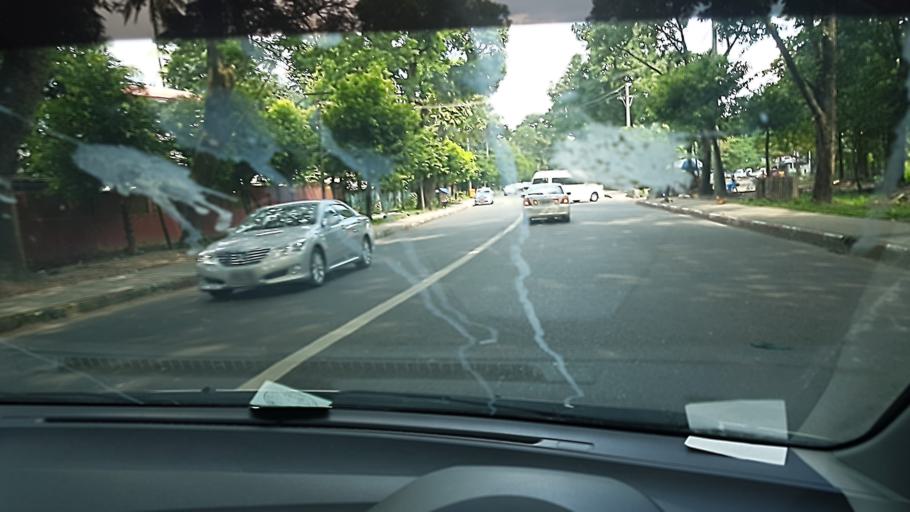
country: MM
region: Yangon
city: Yangon
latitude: 16.7899
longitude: 96.1677
